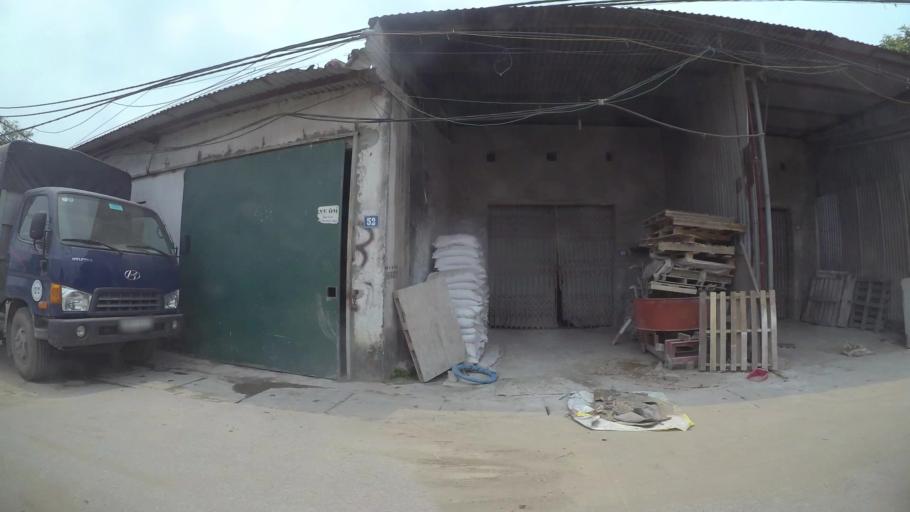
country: VN
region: Ha Noi
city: Ha Dong
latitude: 20.9925
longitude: 105.7407
